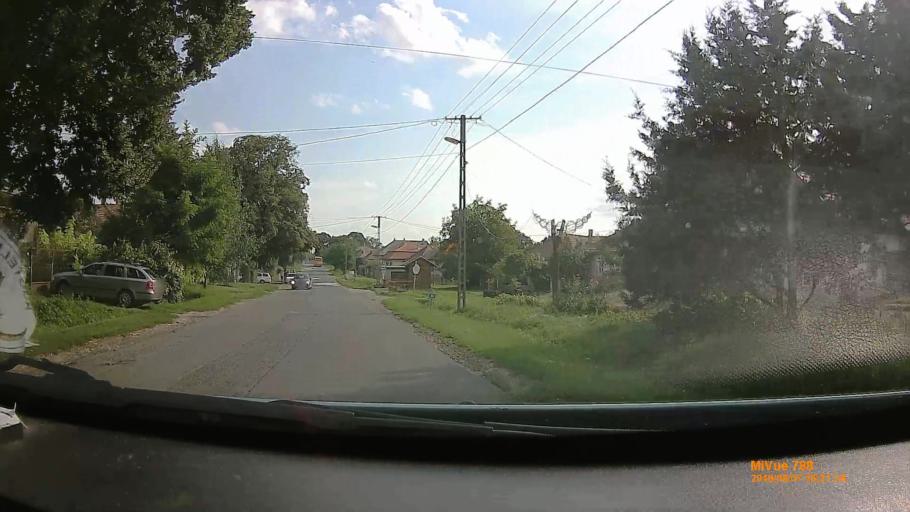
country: HU
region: Borsod-Abauj-Zemplen
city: Gonc
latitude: 48.4471
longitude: 21.2398
